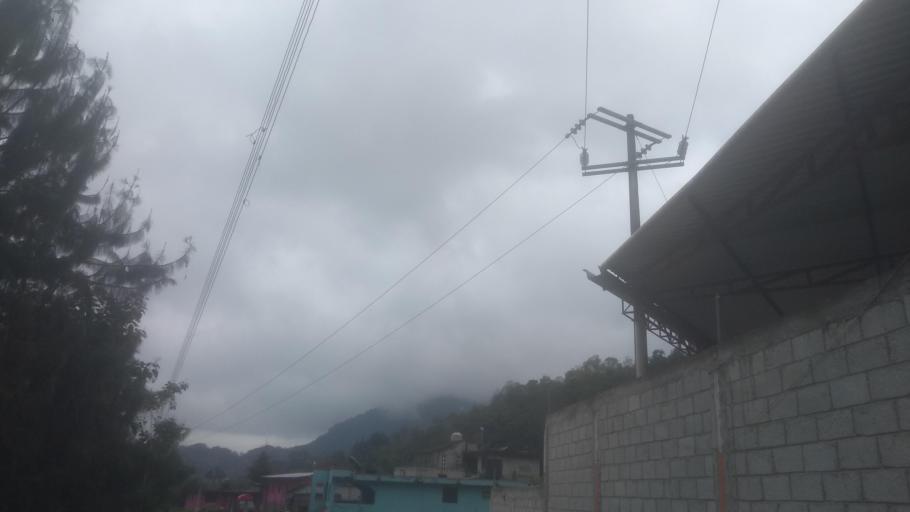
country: MX
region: Veracruz
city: Chocaman
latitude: 18.9964
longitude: -97.0584
